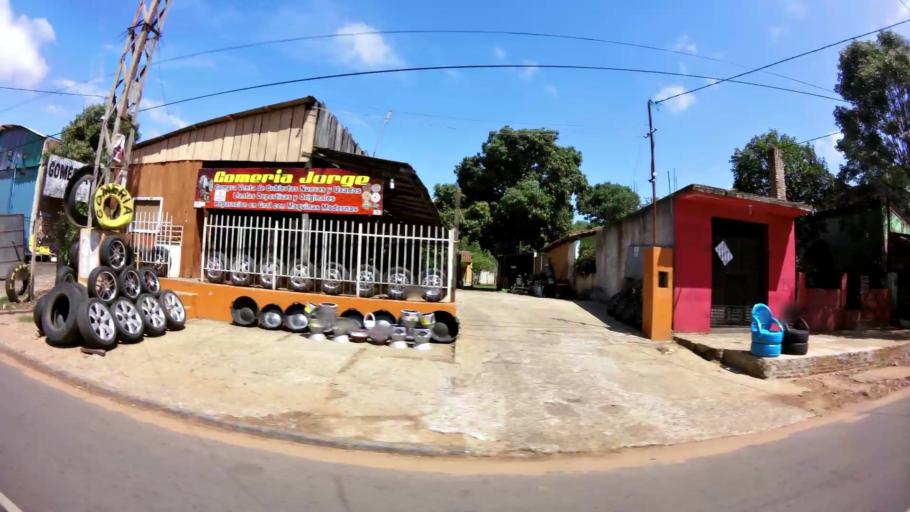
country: PY
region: Central
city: San Lorenzo
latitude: -25.3238
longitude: -57.5090
